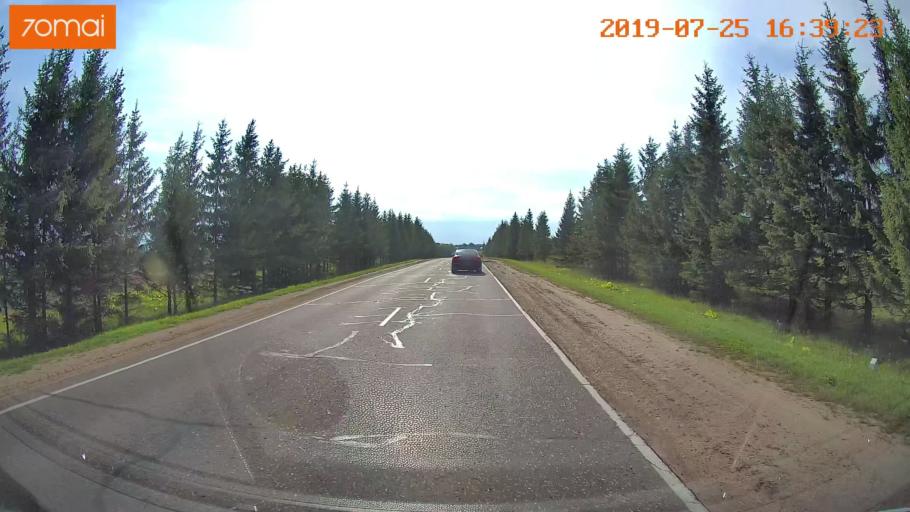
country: RU
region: Ivanovo
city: Privolzhsk
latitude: 57.3870
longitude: 41.3281
